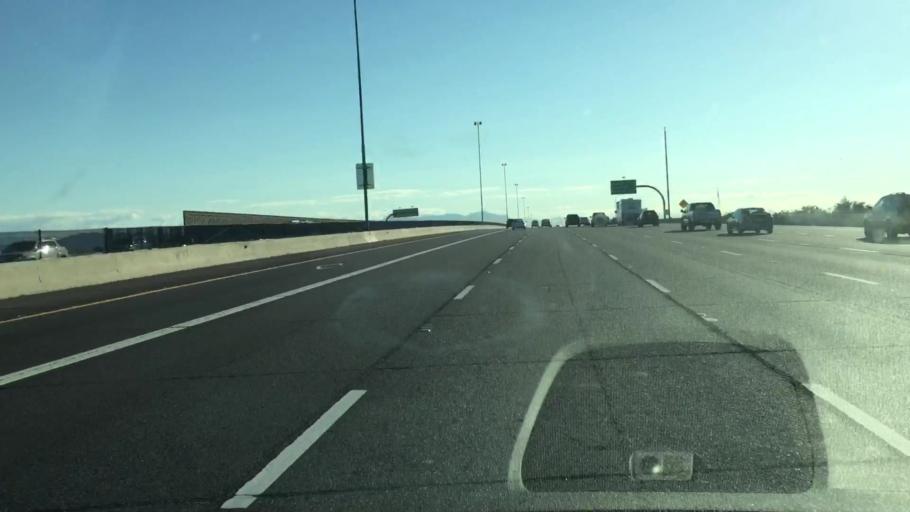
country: US
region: Arizona
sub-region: Maricopa County
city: Mesa
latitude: 33.3847
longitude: -111.8348
